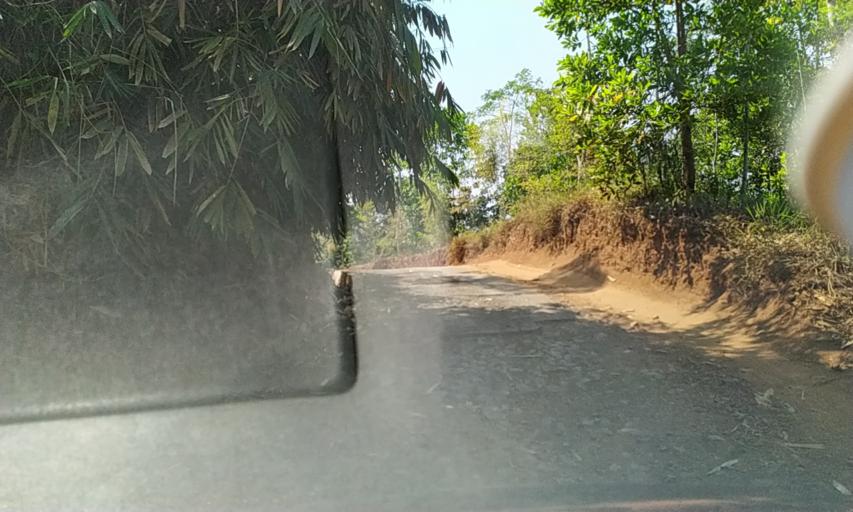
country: ID
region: Central Java
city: Cilumping
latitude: -7.1924
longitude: 108.6138
